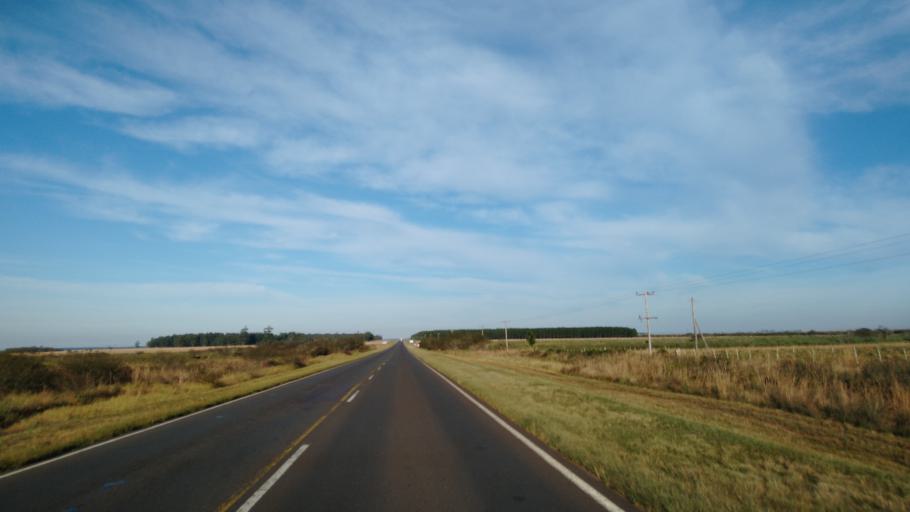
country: AR
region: Corrientes
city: La Cruz
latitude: -29.2408
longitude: -56.7305
